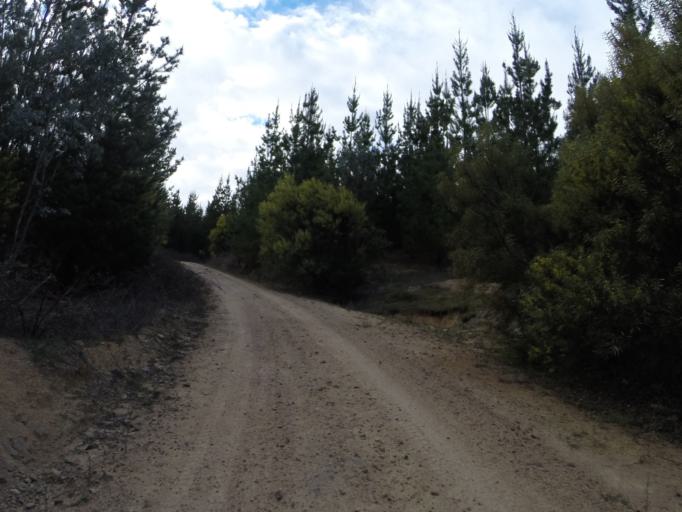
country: AU
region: Australian Capital Territory
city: Macquarie
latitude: -35.3478
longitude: 148.9499
